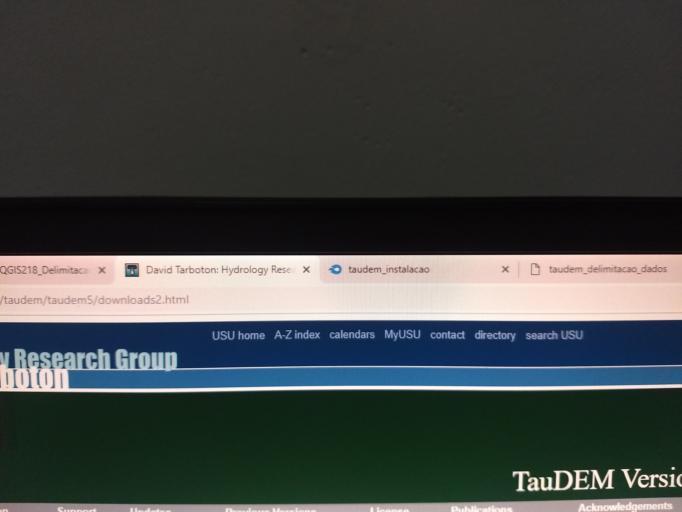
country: BR
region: Espirito Santo
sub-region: Cachoeiro De Itapemirim
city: Cachoeiro de Itapemirim
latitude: -20.8389
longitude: -41.1164
